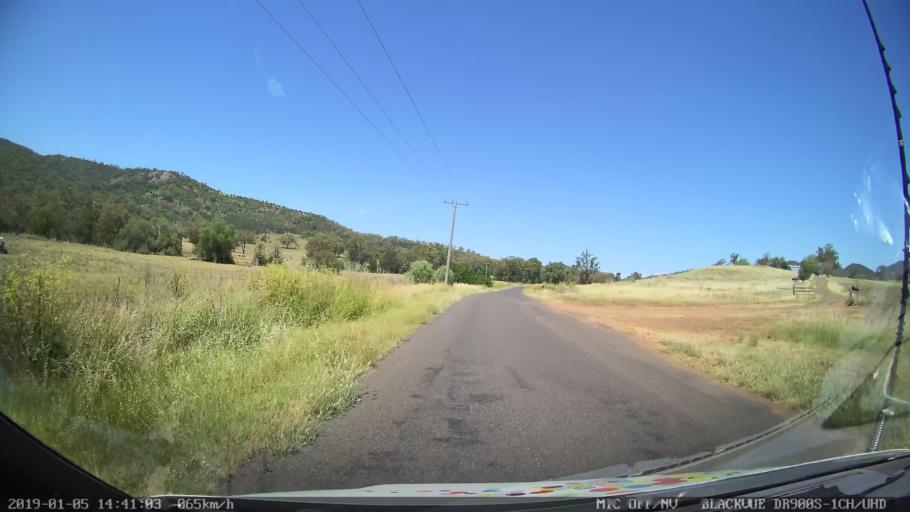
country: AU
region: New South Wales
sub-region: Tamworth Municipality
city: Phillip
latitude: -31.2608
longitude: 150.7203
